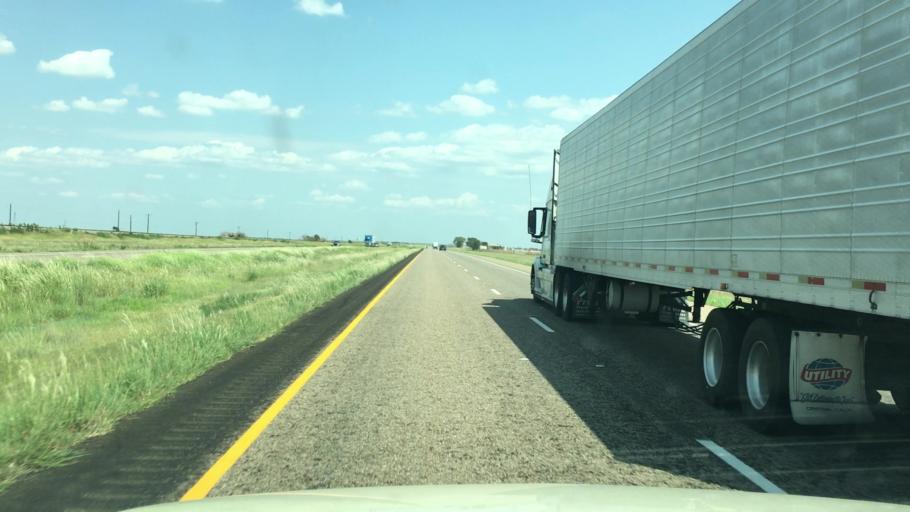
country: US
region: Texas
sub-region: Armstrong County
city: Claude
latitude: 35.0319
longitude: -101.1285
